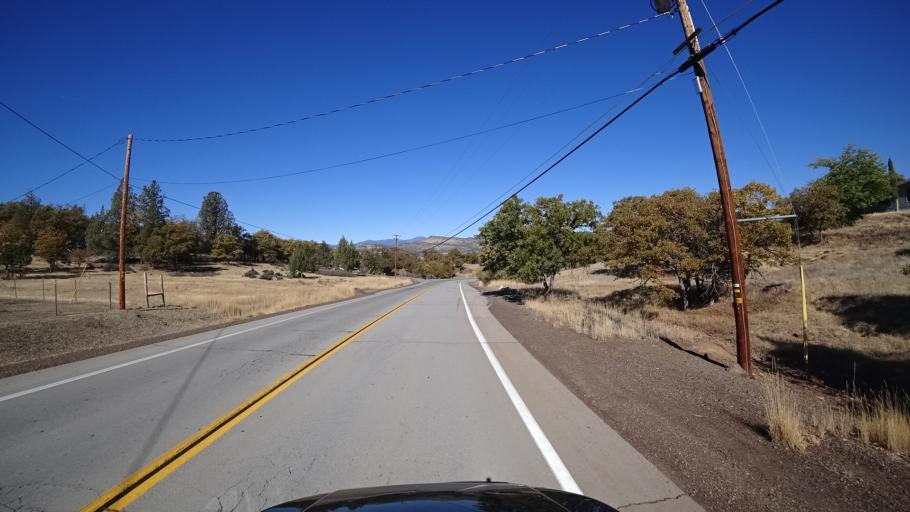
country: US
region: California
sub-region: Siskiyou County
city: Montague
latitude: 41.8823
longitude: -122.4849
